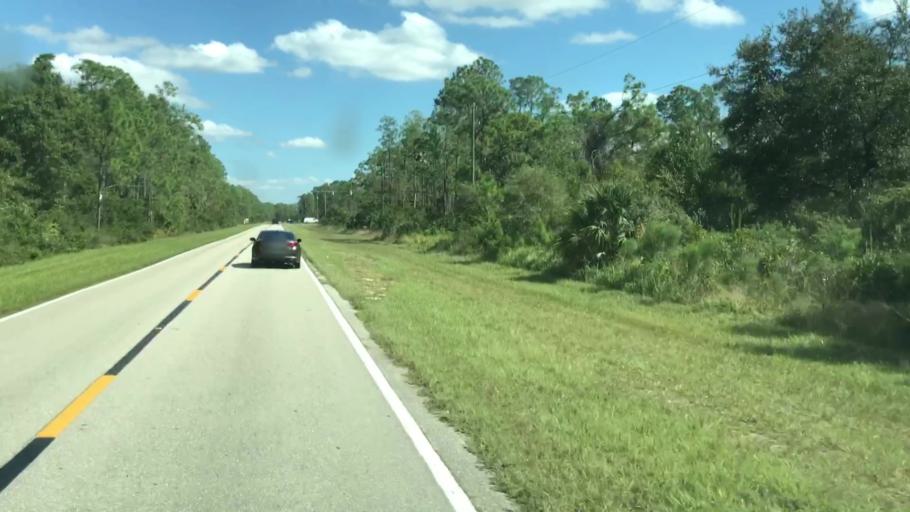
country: US
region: Florida
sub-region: Lee County
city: Alva
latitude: 26.6775
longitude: -81.6141
